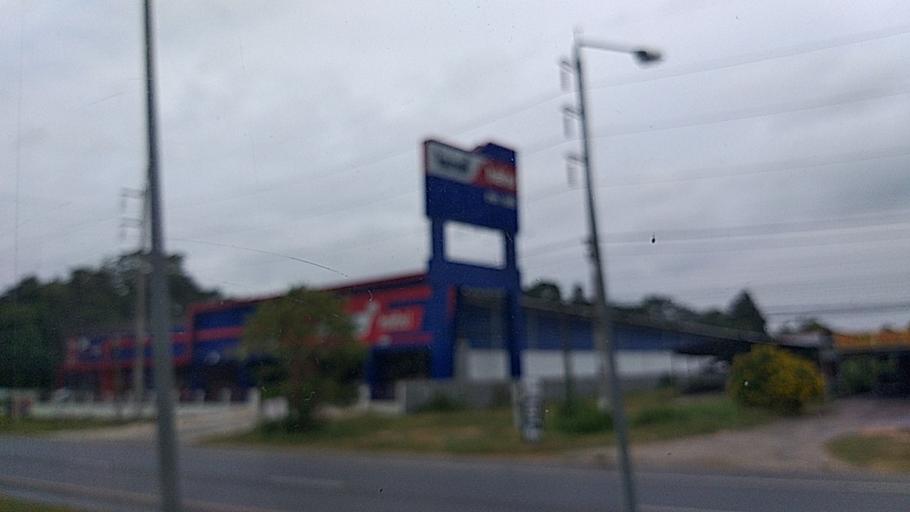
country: TH
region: Maha Sarakham
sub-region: Amphoe Borabue
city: Borabue
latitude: 16.0481
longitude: 103.1264
